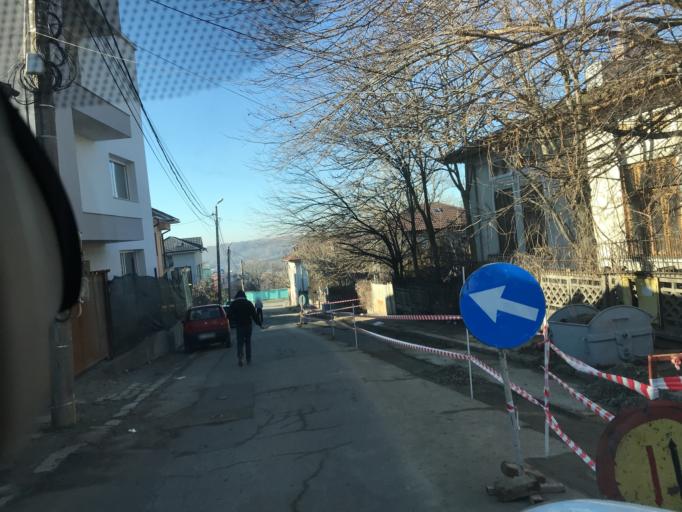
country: RO
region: Olt
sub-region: Municipiul Slatina
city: Slatina
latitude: 44.4287
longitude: 24.3622
